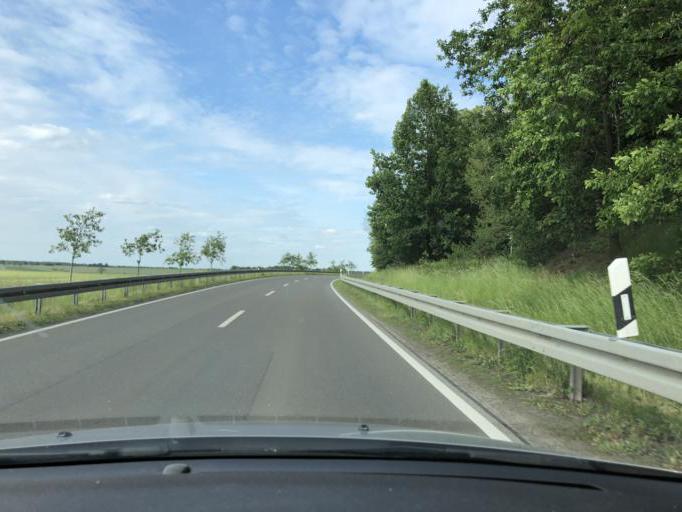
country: DE
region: Saxony
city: Brandis
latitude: 51.2975
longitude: 12.6467
